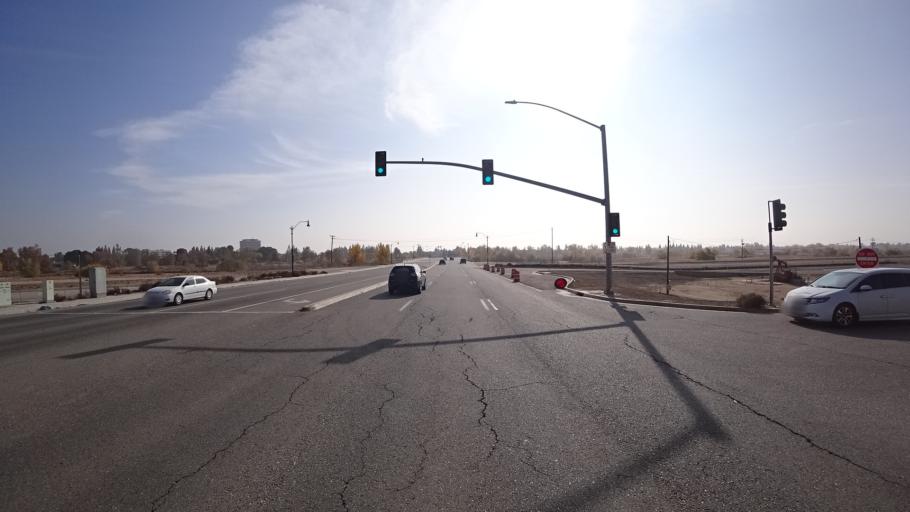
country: US
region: California
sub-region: Kern County
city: Greenacres
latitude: 35.3701
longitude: -119.0660
